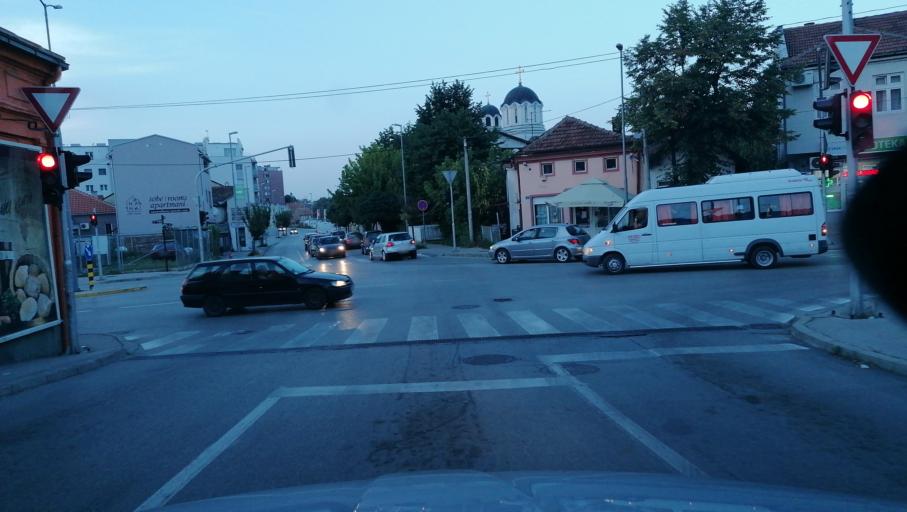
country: RS
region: Central Serbia
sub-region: Kolubarski Okrug
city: Valjevo
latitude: 44.2664
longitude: 19.8896
